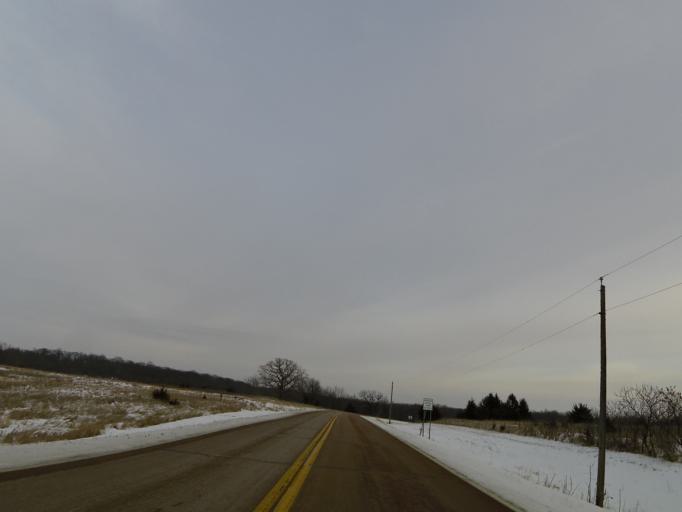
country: US
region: Minnesota
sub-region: Carver County
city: Victoria
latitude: 44.8722
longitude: -93.6834
